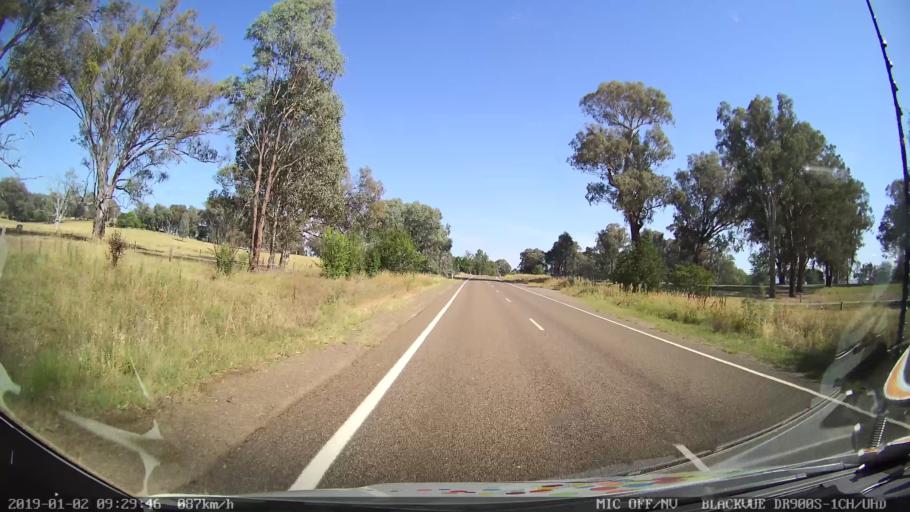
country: AU
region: New South Wales
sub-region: Tumut Shire
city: Tumut
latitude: -35.3350
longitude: 148.2396
